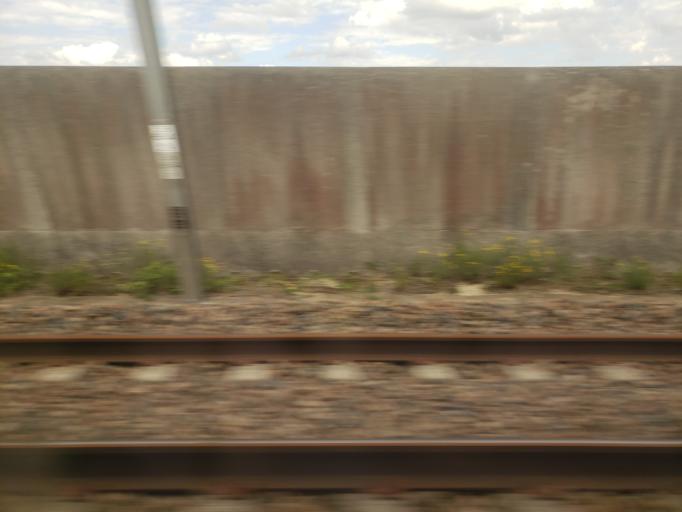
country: FR
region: Ile-de-France
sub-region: Departement de Seine-et-Marne
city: Moisenay
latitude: 48.5869
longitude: 2.7278
